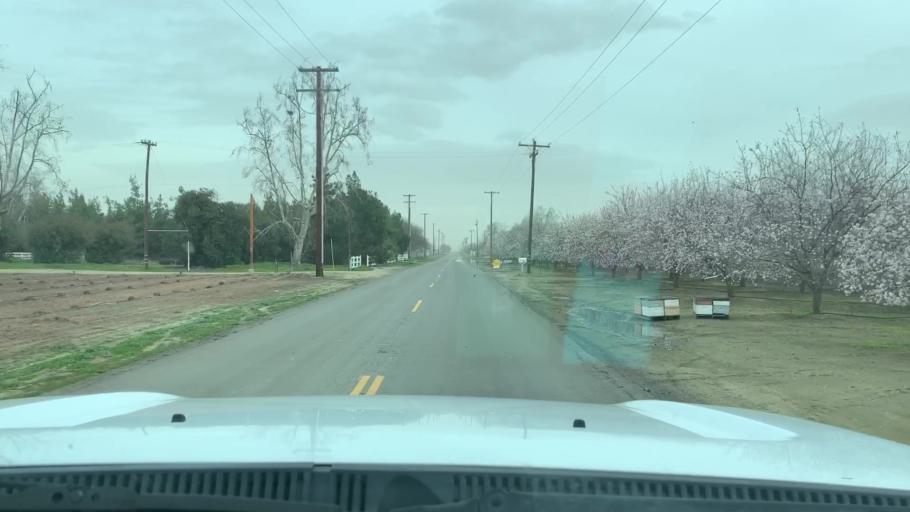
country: US
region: California
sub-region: Kern County
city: Shafter
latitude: 35.5292
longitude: -119.2680
